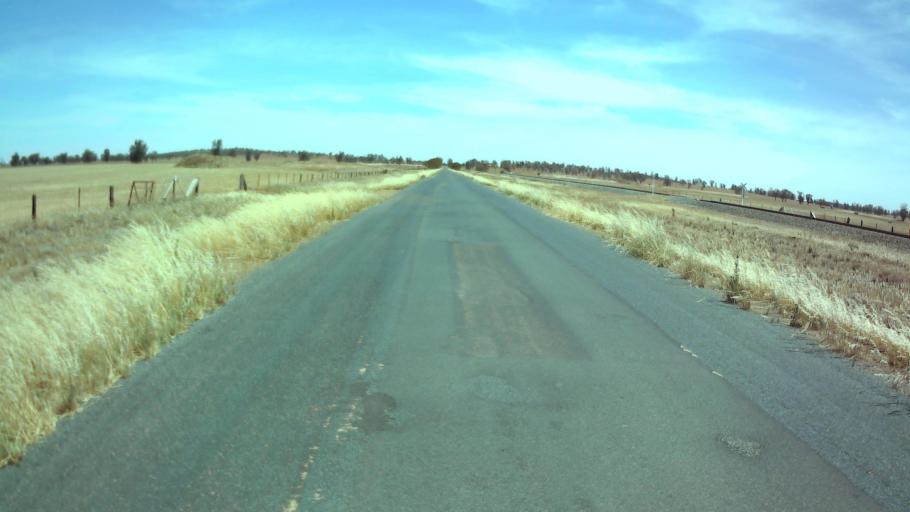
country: AU
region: New South Wales
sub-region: Weddin
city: Grenfell
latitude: -33.7572
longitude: 147.7625
